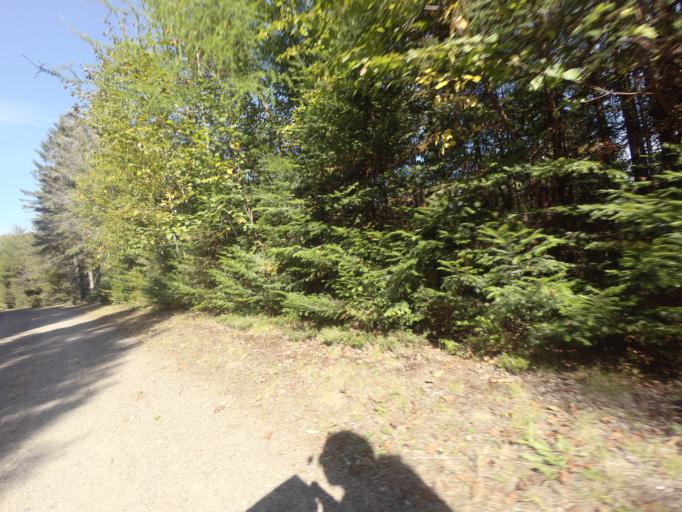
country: CA
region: Quebec
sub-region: Laurentides
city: Sainte-Agathe-des-Monts
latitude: 46.1034
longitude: -74.3644
